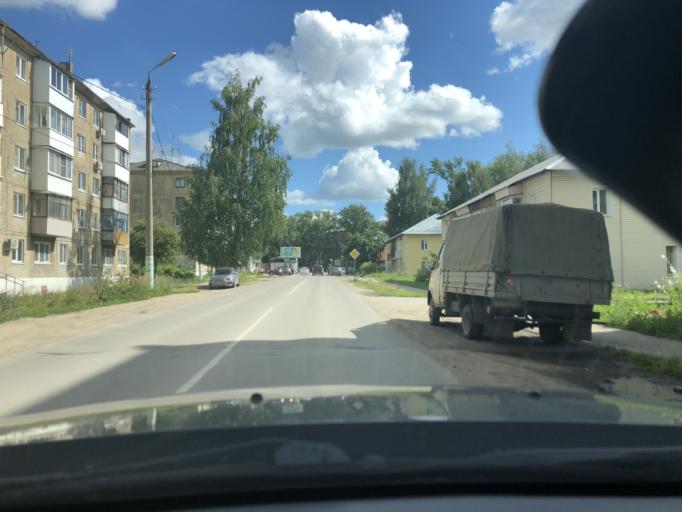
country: RU
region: Tula
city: Kimovsk
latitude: 53.9752
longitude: 38.5305
